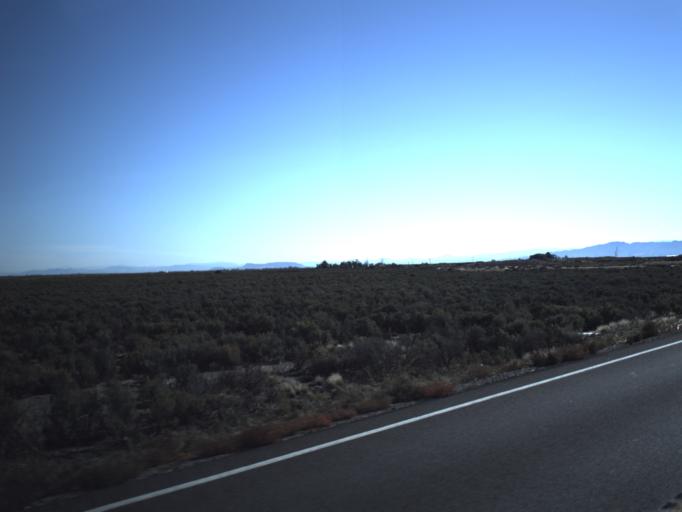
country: US
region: Utah
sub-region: Washington County
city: Enterprise
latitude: 37.7706
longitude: -113.8298
